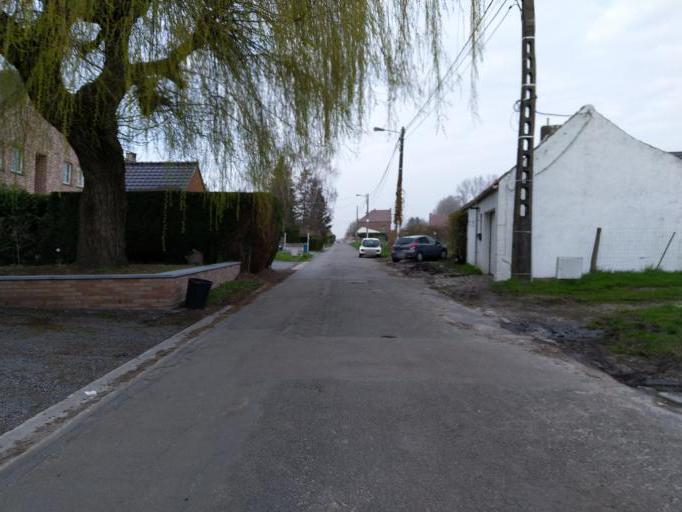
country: BE
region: Wallonia
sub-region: Province du Hainaut
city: Mons
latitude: 50.5131
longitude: 3.9926
